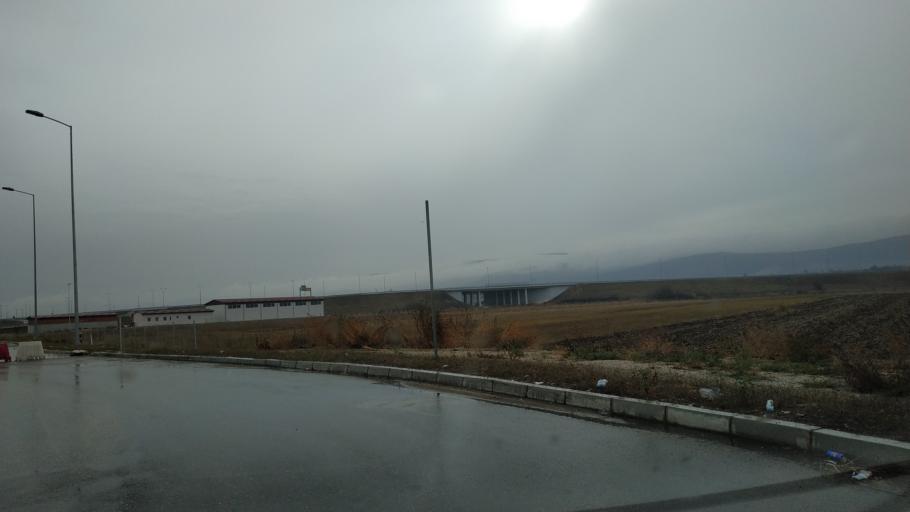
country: RS
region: Central Serbia
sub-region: Pirotski Okrug
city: Pirot
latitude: 43.1244
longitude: 22.6179
